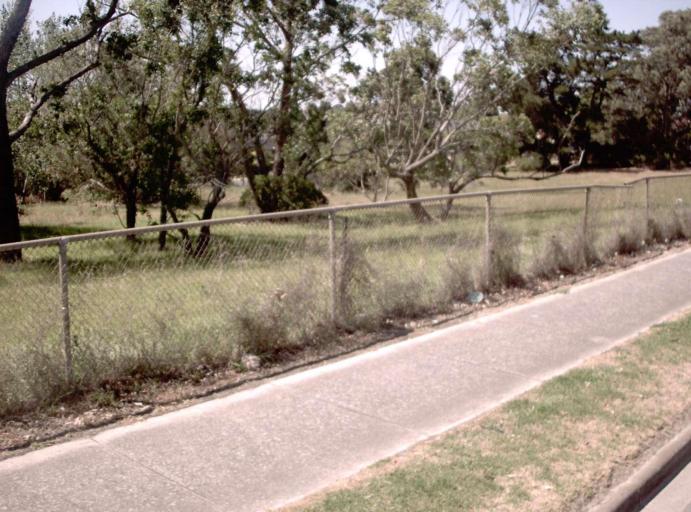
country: AU
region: Victoria
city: Burwood East
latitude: -37.8517
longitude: 145.1368
